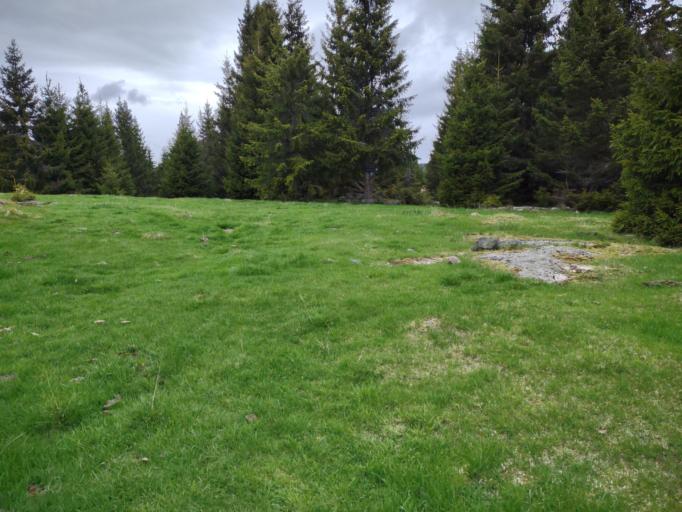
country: NO
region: Oppland
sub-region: Lunner
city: Grua
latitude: 60.3223
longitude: 10.7929
